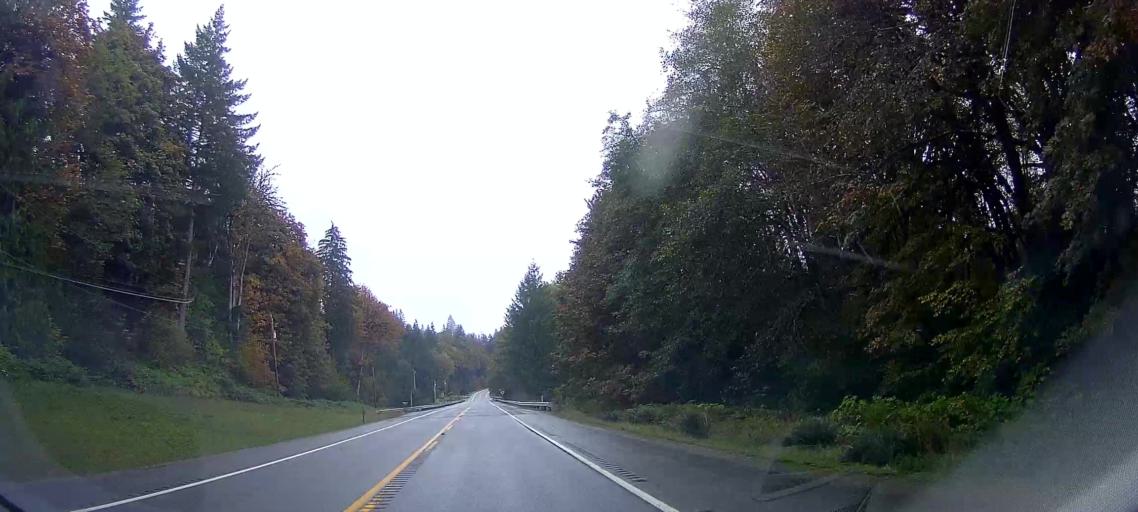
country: US
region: Washington
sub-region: Snohomish County
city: Darrington
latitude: 48.5064
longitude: -121.6546
